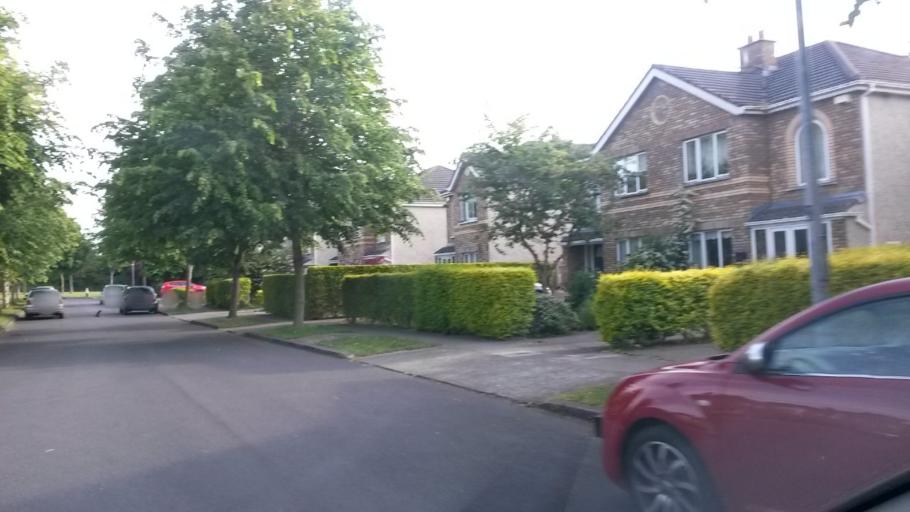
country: IE
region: Leinster
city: Hartstown
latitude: 53.3843
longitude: -6.4114
